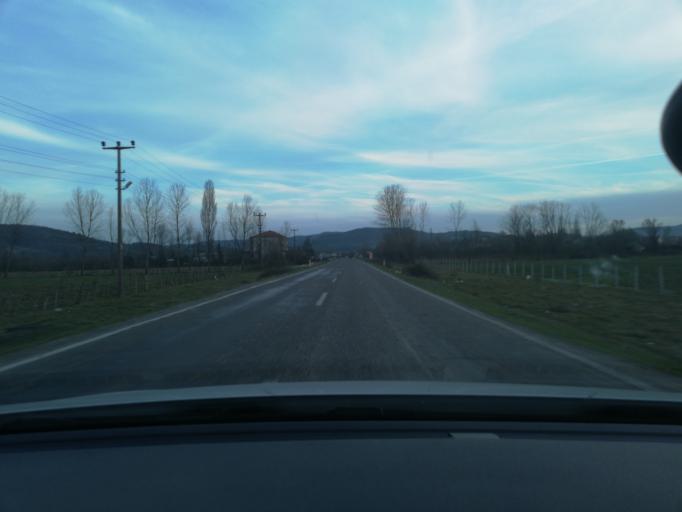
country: TR
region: Zonguldak
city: Saltukova
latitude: 41.5184
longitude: 32.1023
